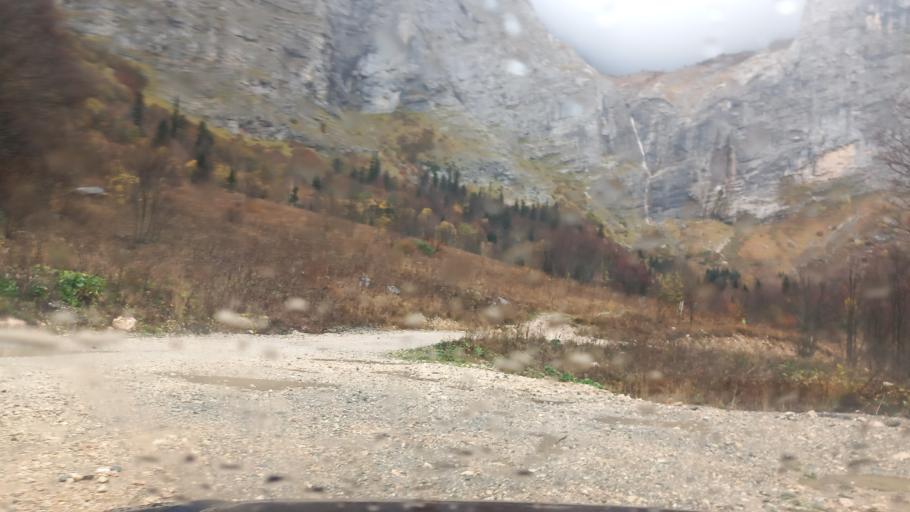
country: RU
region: Krasnodarskiy
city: Dagomys
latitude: 43.9791
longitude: 39.8718
